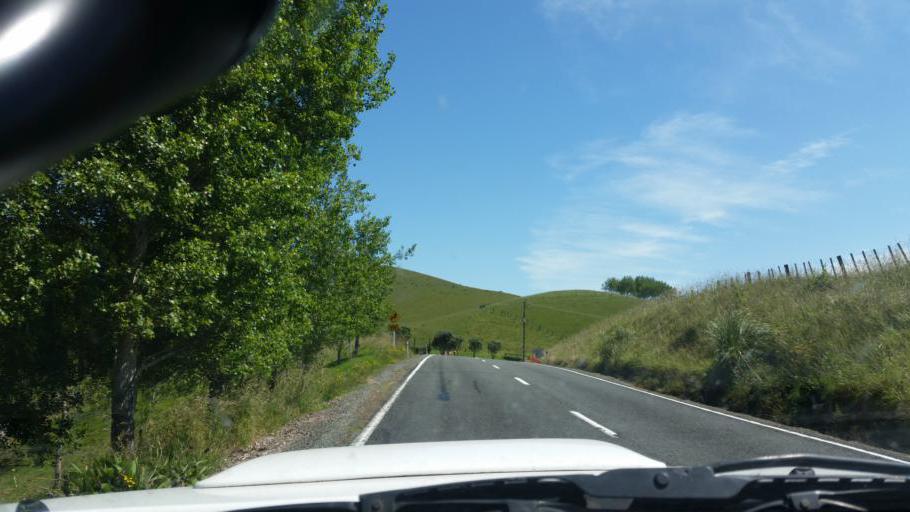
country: NZ
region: Auckland
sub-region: Auckland
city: Wellsford
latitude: -36.2002
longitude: 174.3964
